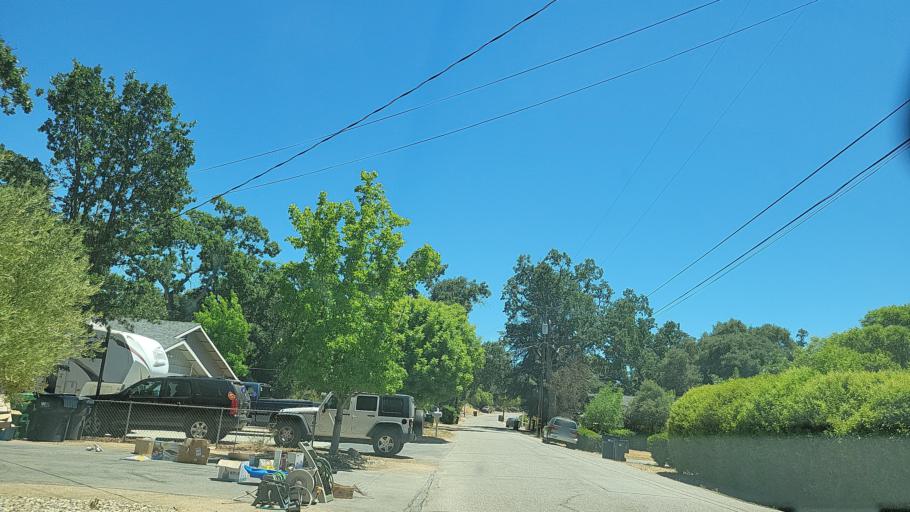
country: US
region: California
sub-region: San Luis Obispo County
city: Atascadero
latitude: 35.4804
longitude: -120.6632
